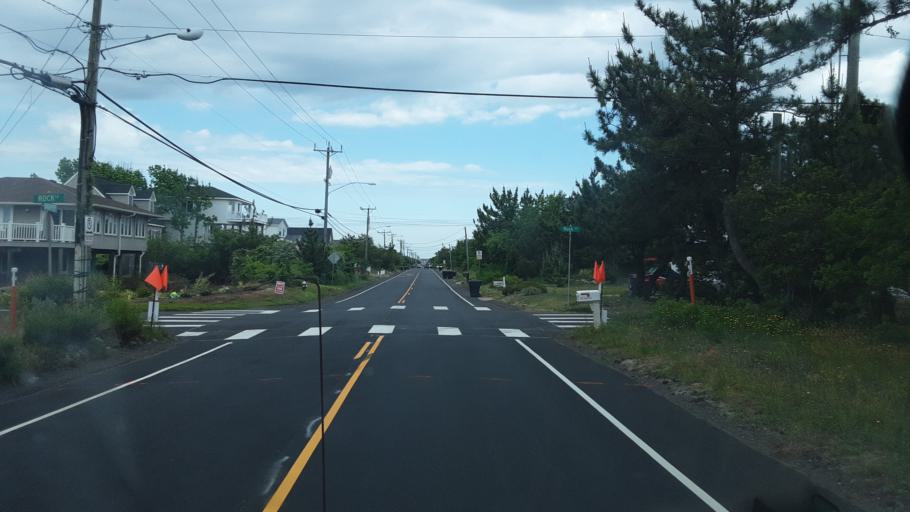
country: US
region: Virginia
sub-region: City of Virginia Beach
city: Virginia Beach
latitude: 36.7247
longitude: -75.9371
